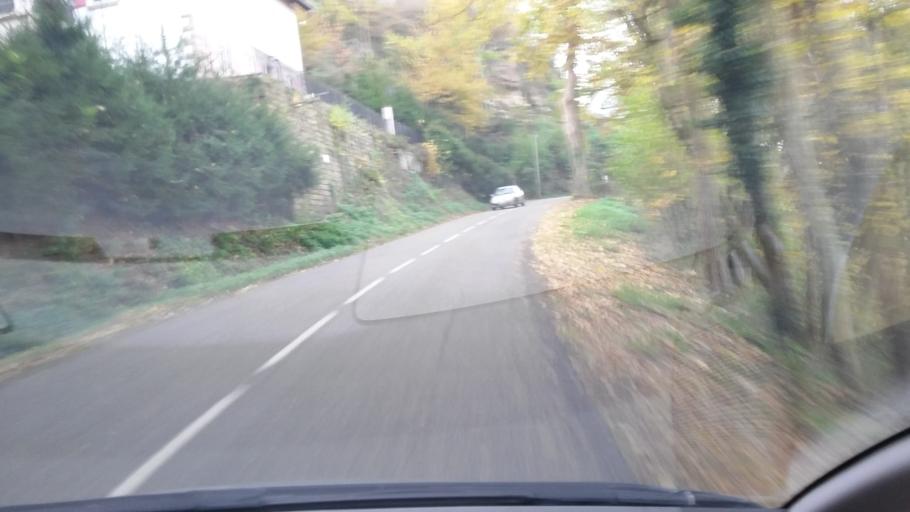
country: FR
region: Alsace
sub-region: Departement du Bas-Rhin
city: Neuwiller-les-Saverne
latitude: 48.8549
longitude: 7.3201
